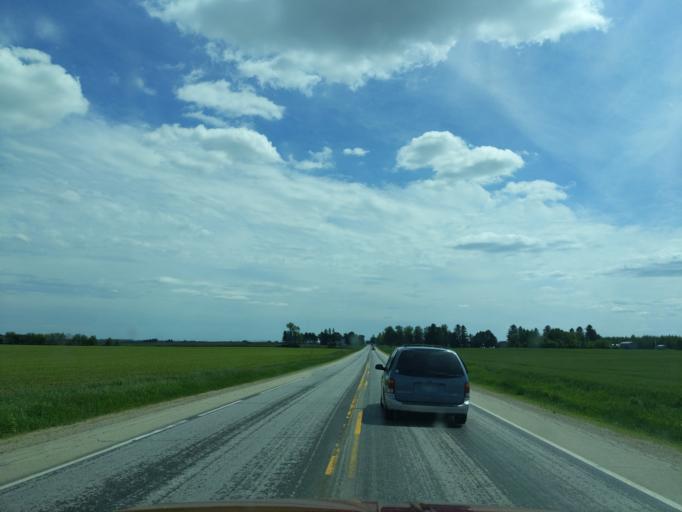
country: US
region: Wisconsin
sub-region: Dane County
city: De Forest
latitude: 43.3212
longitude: -89.3254
